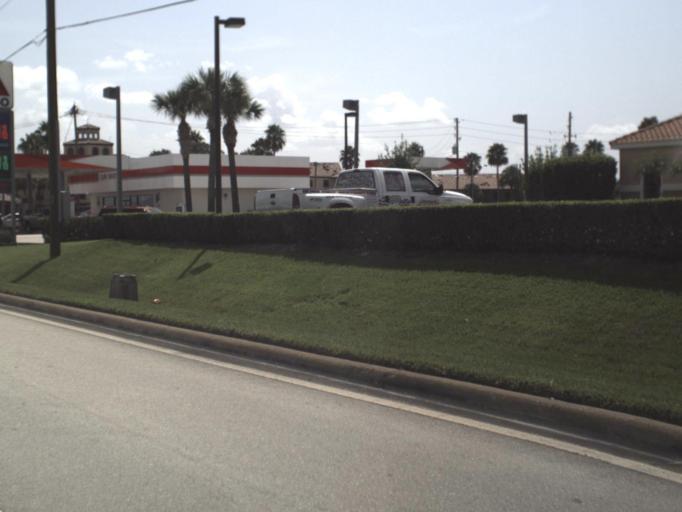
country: US
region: Florida
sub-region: Highlands County
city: Sebring
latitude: 27.4726
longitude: -81.4668
